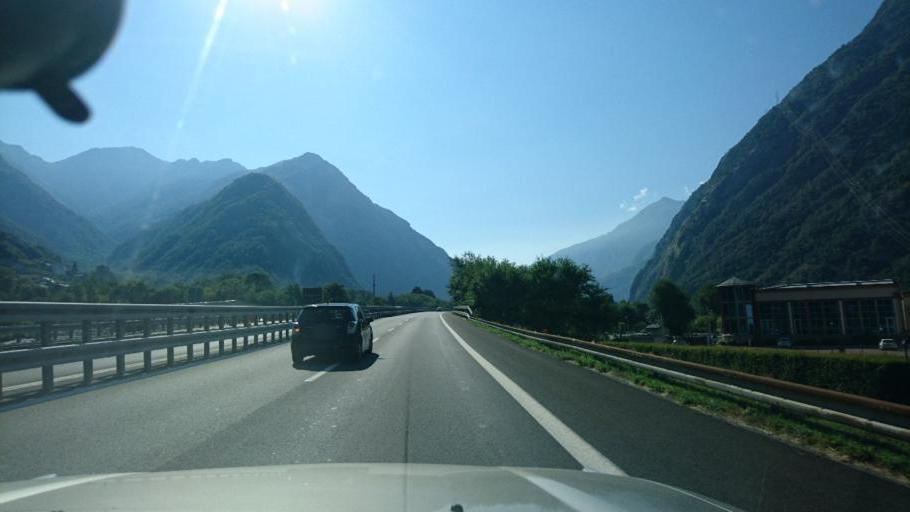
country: IT
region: Aosta Valley
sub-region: Valle d'Aosta
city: Arnad
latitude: 45.6421
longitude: 7.7176
